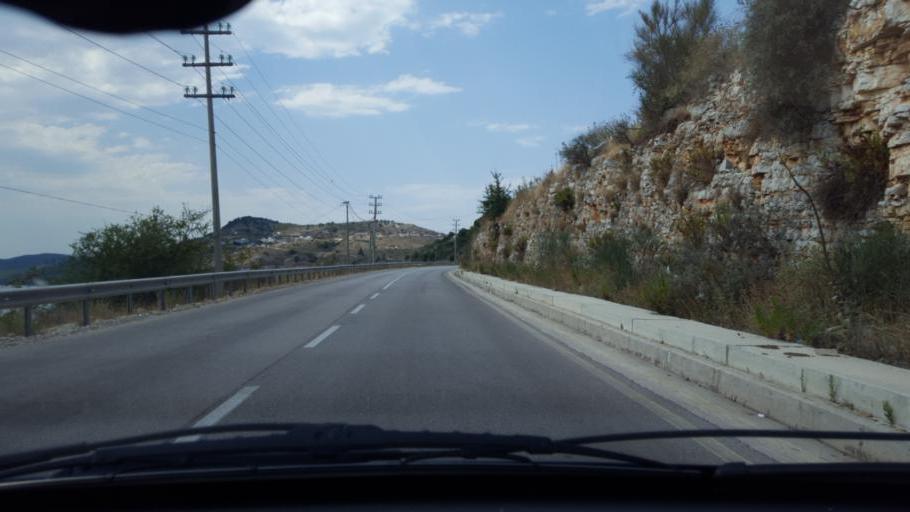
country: AL
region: Vlore
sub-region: Rrethi i Sarandes
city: Sarande
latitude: 39.8131
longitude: 20.0135
